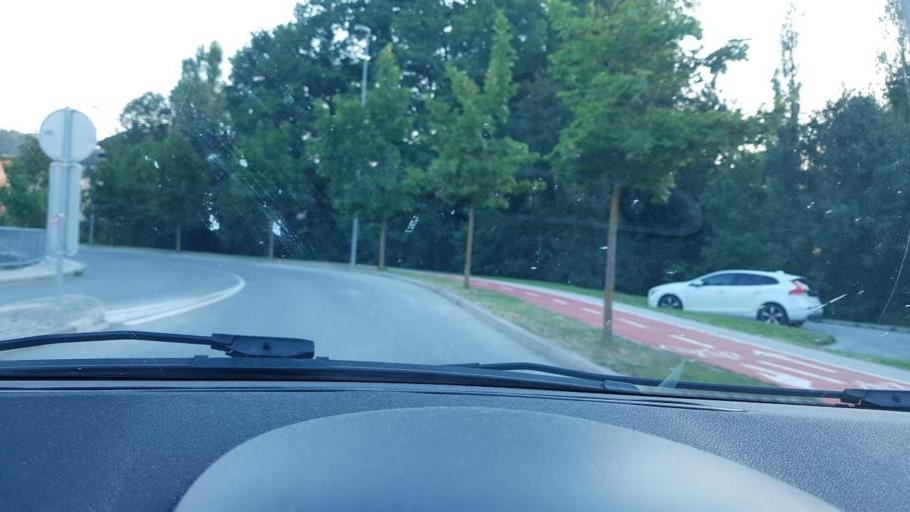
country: SI
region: Rogaska Slatina
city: Rogaska Slatina
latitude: 46.2454
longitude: 15.6262
